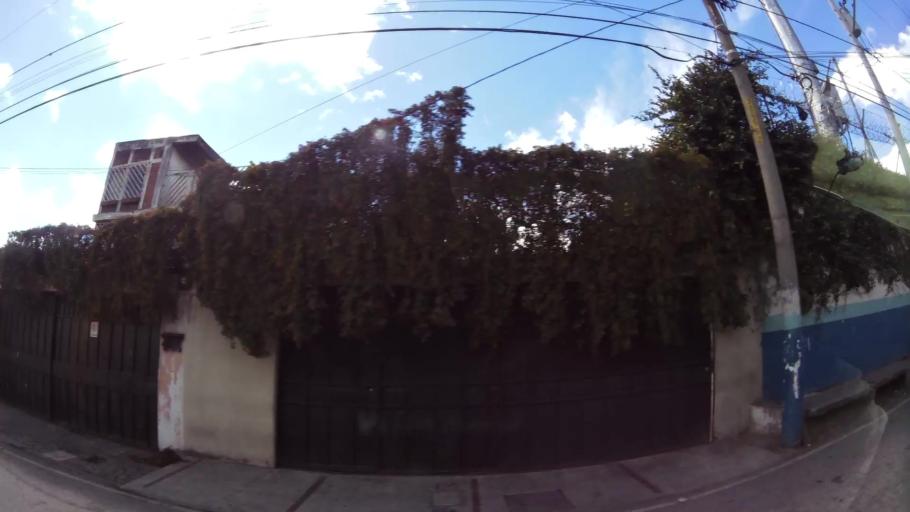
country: GT
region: Guatemala
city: Guatemala City
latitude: 14.6052
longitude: -90.5322
